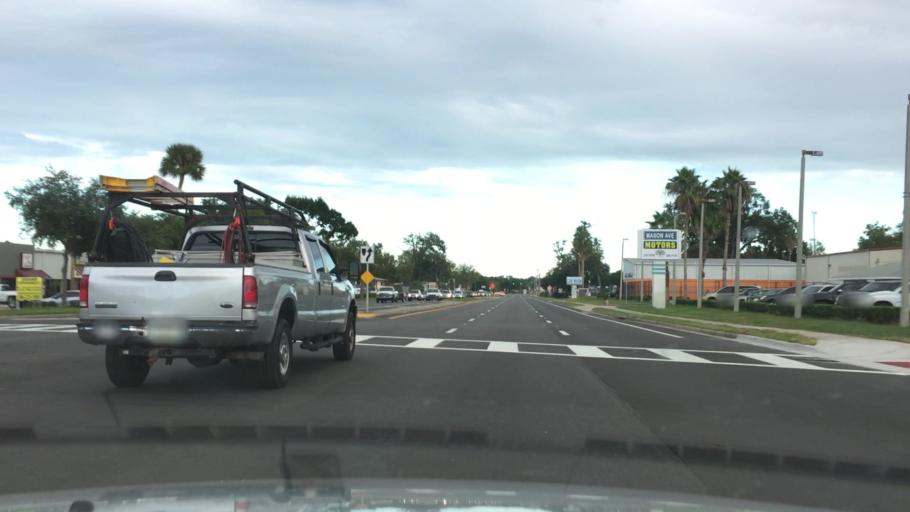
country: US
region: Florida
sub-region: Volusia County
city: Holly Hill
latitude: 29.2444
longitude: -81.0640
